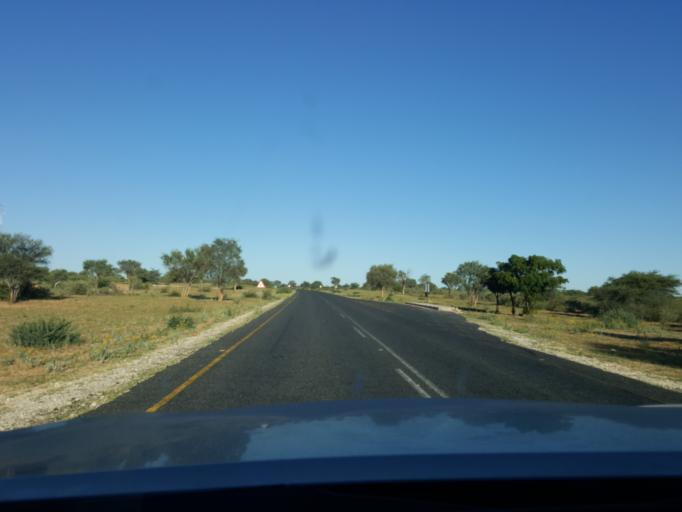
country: BW
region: Southern
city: Khakhea
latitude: -24.2300
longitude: 23.2462
